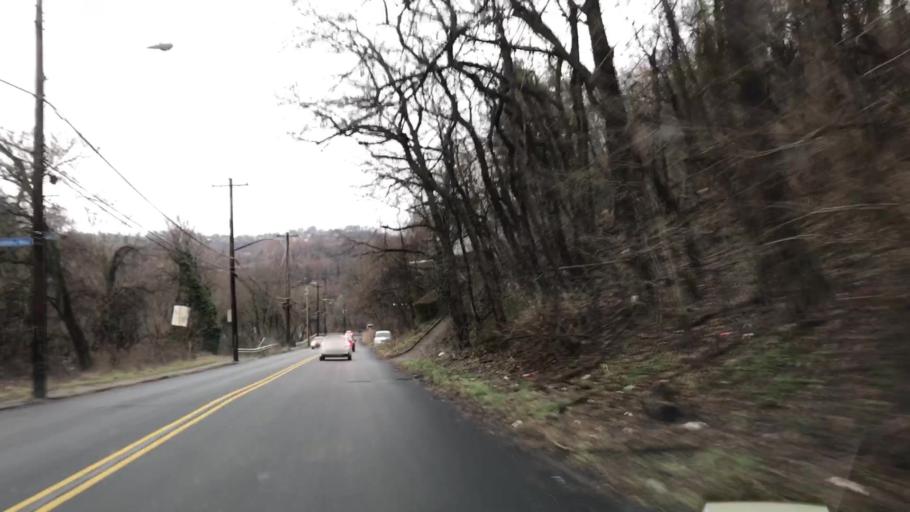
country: US
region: Pennsylvania
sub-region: Allegheny County
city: Green Tree
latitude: 40.4300
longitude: -80.0395
